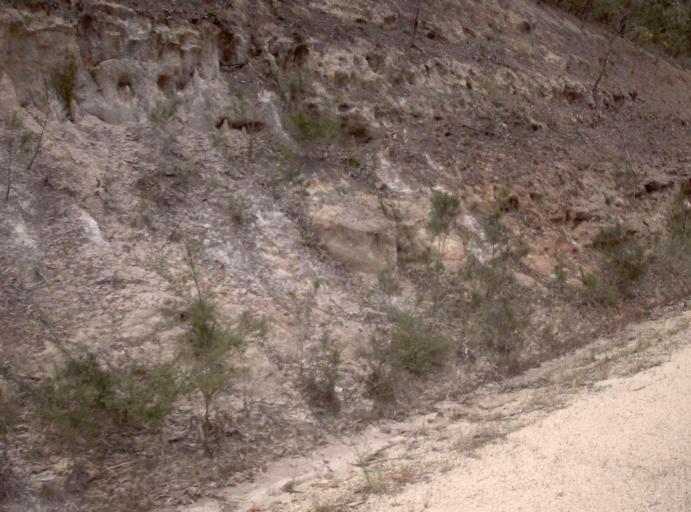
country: AU
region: New South Wales
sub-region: Bega Valley
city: Eden
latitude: -37.3935
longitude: 149.6761
